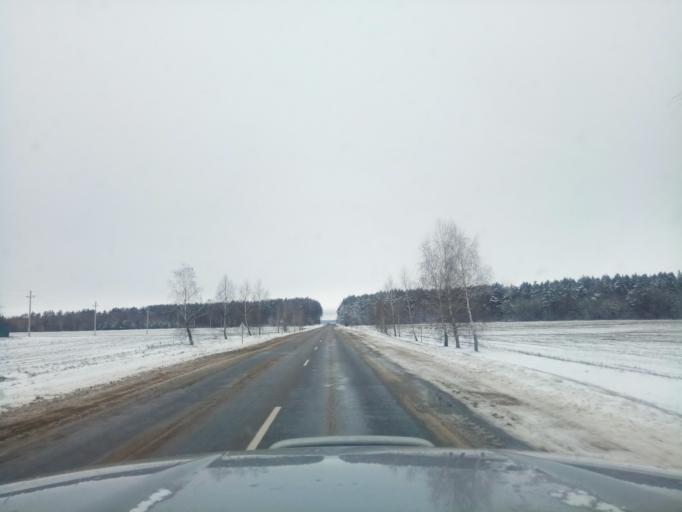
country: BY
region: Minsk
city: Kapyl'
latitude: 53.1553
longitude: 27.1149
